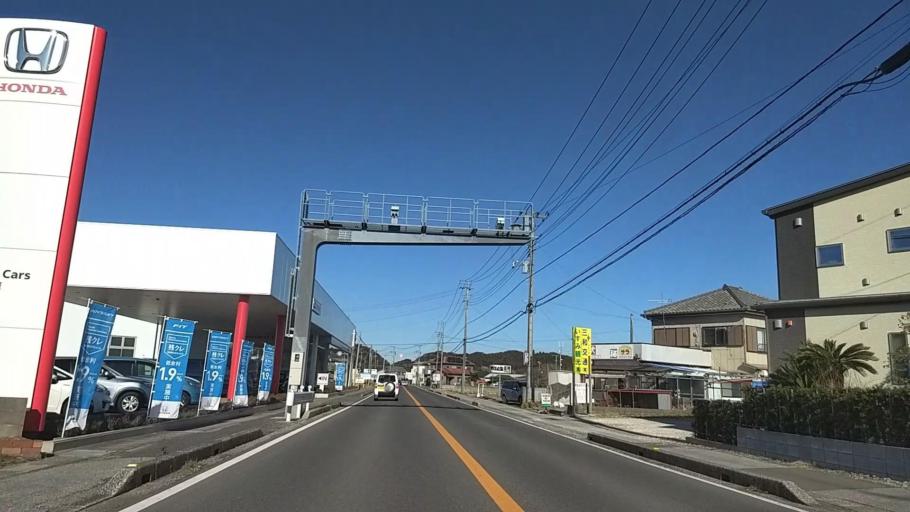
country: JP
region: Chiba
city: Ohara
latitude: 35.3033
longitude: 140.3998
